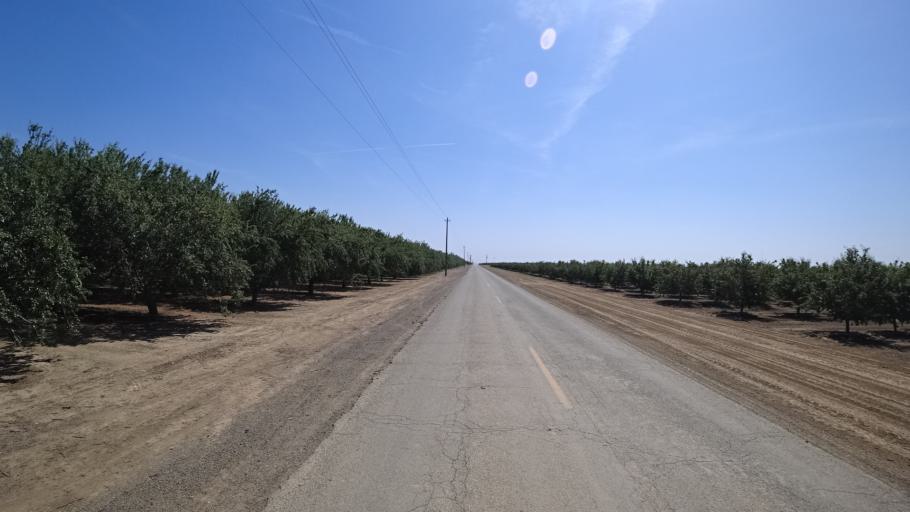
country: US
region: California
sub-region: Kings County
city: Kettleman City
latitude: 36.0943
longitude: -119.9988
